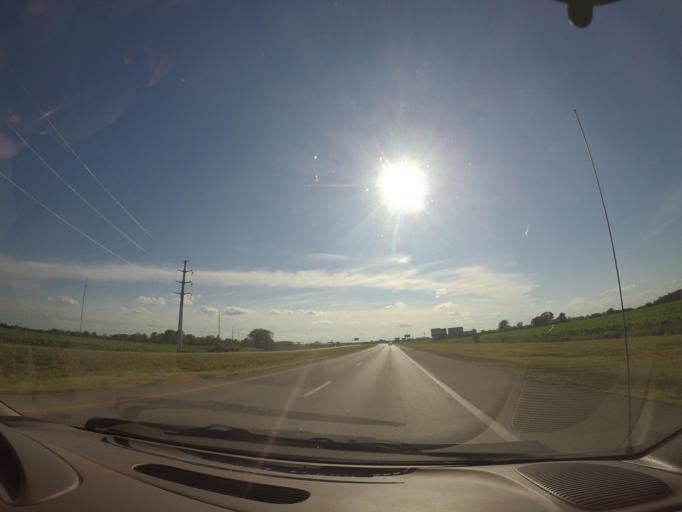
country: US
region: Ohio
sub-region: Henry County
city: Napoleon
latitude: 41.4169
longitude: -84.0838
